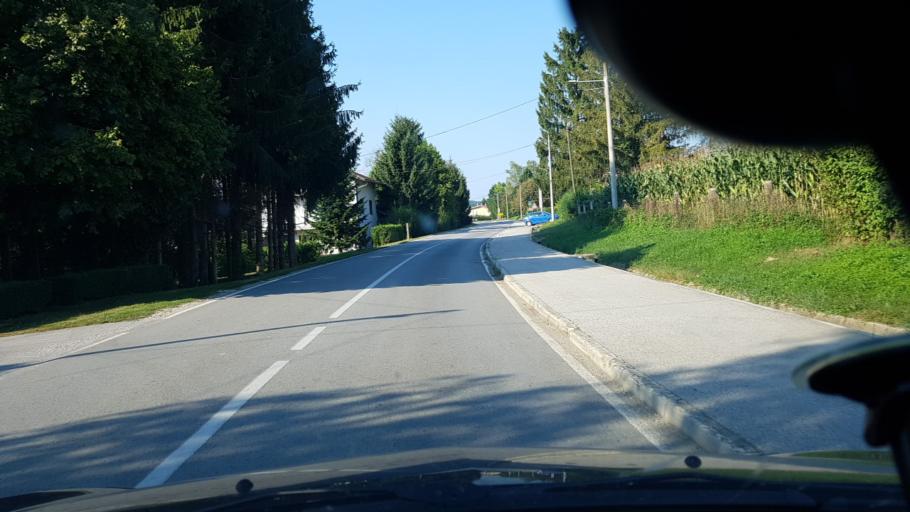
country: HR
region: Zagrebacka
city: Pojatno
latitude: 45.9561
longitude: 15.7317
